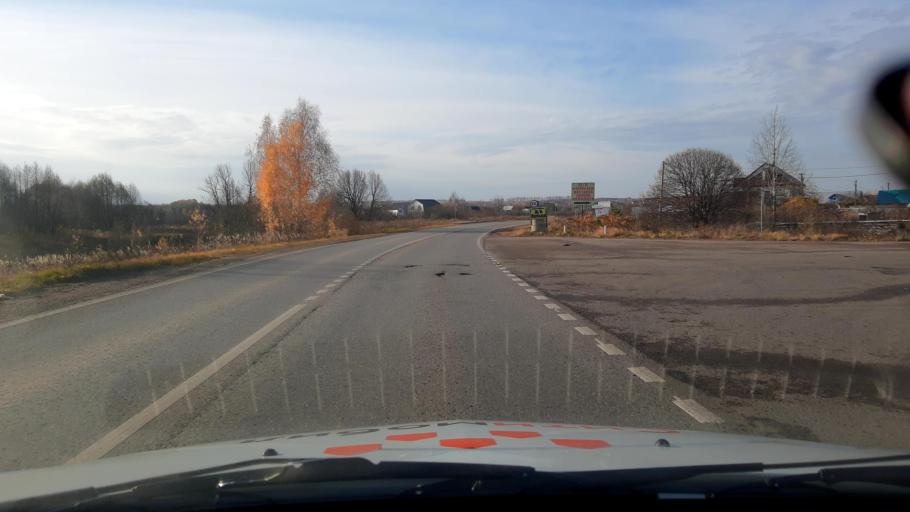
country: RU
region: Bashkortostan
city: Kabakovo
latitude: 54.7261
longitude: 56.1898
